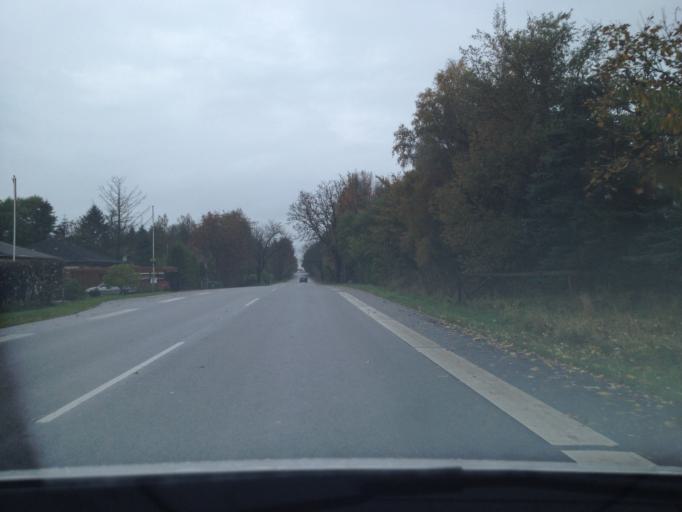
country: DK
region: Capital Region
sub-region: Fredensborg Kommune
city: Fredensborg
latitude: 55.9361
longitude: 12.4338
